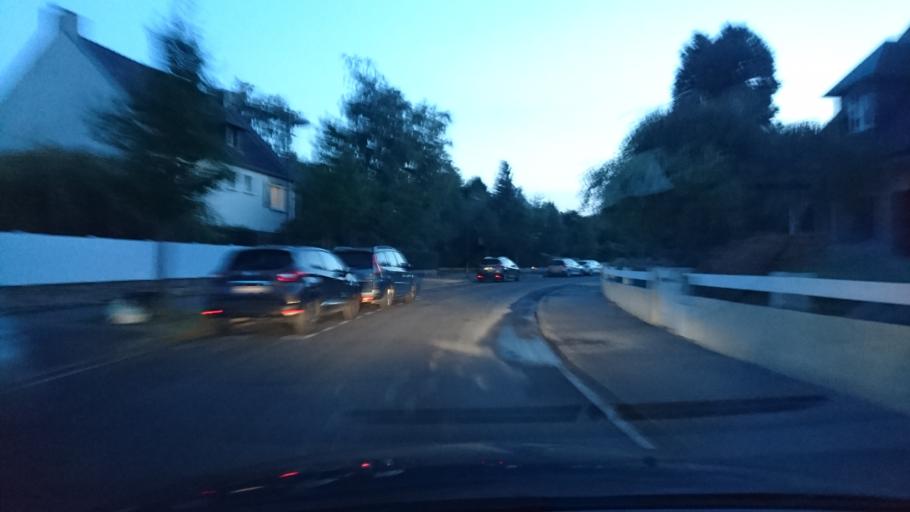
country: FR
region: Brittany
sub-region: Departement d'Ille-et-Vilaine
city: Saint-Jacques-de-la-Lande
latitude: 48.0814
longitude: -1.6907
